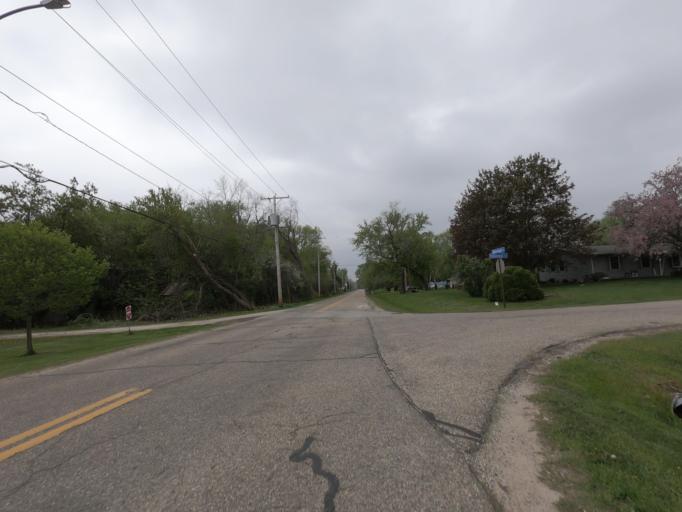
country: US
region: Wisconsin
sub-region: Jefferson County
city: Jefferson
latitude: 43.0272
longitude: -88.8094
